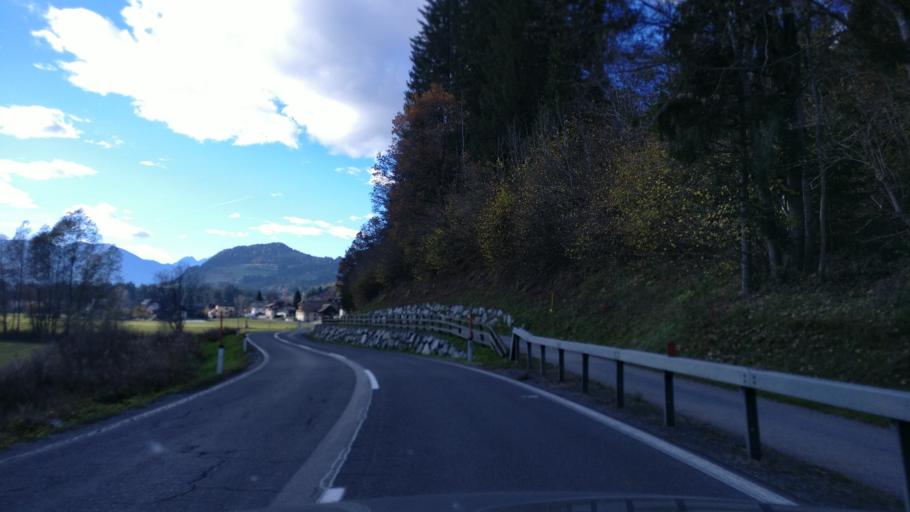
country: AT
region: Carinthia
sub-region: Politischer Bezirk Spittal an der Drau
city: Berg im Drautal
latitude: 46.7436
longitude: 13.1138
